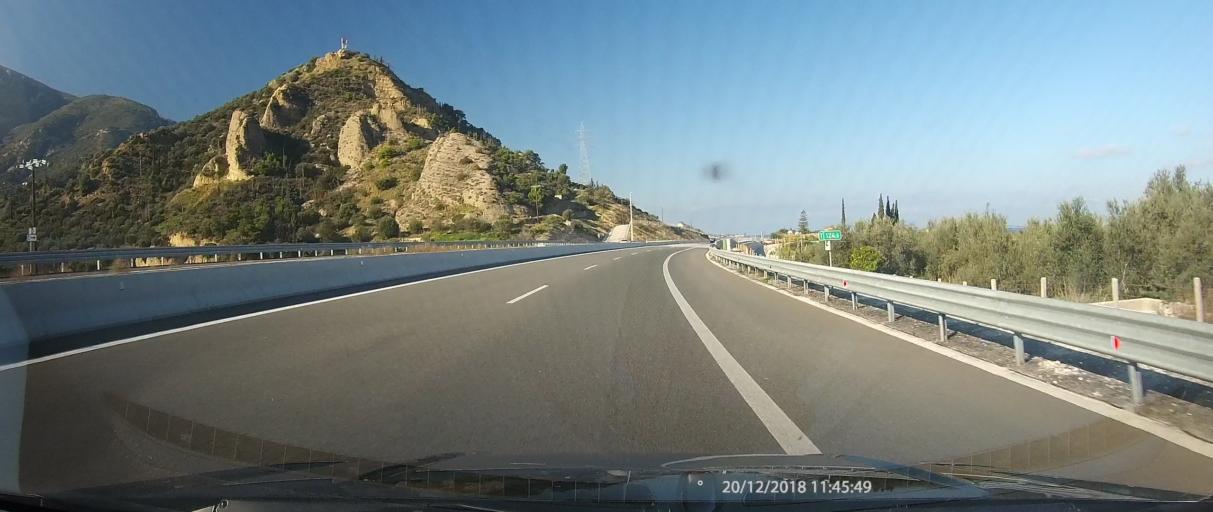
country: GR
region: Peloponnese
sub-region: Nomos Korinthias
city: Xylokastro
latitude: 38.0953
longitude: 22.5641
